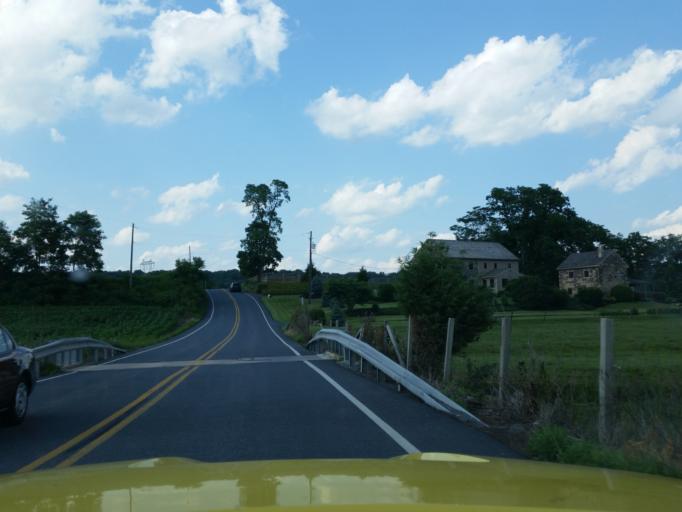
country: US
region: Pennsylvania
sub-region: Lebanon County
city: Campbelltown
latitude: 40.2134
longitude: -76.5060
